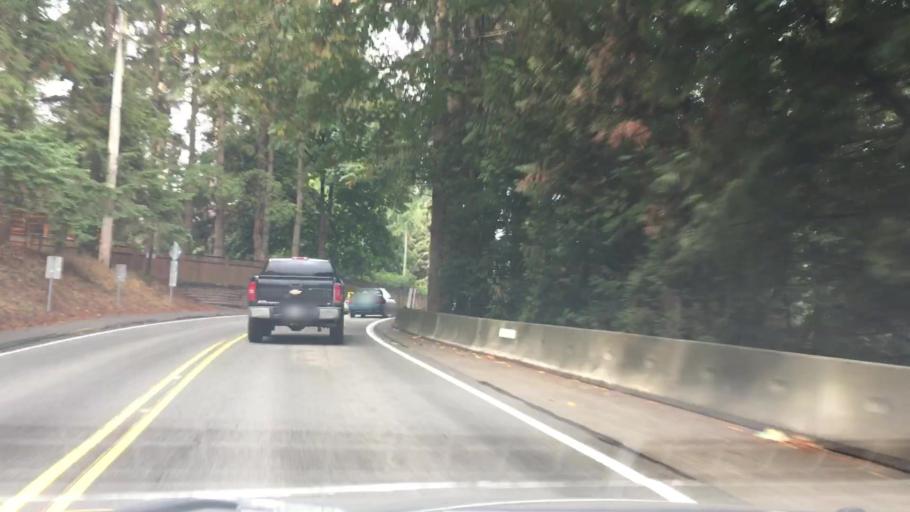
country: CA
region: British Columbia
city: Langley
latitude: 49.1036
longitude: -122.5527
